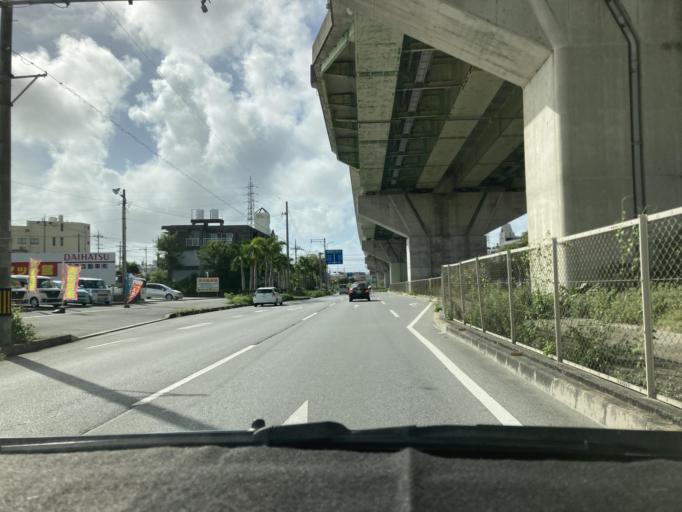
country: JP
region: Okinawa
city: Naha-shi
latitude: 26.2017
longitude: 127.7393
